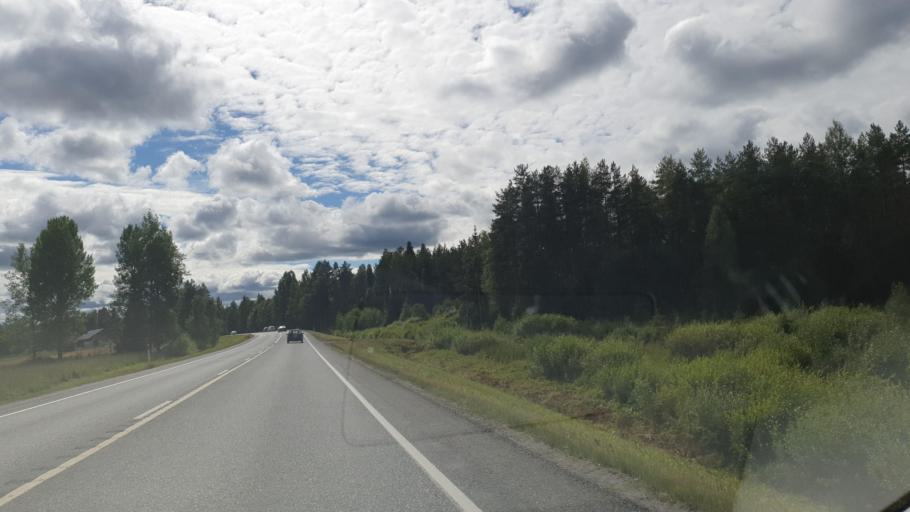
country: FI
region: Kainuu
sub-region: Kajaani
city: Kajaani
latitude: 64.1478
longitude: 27.5051
